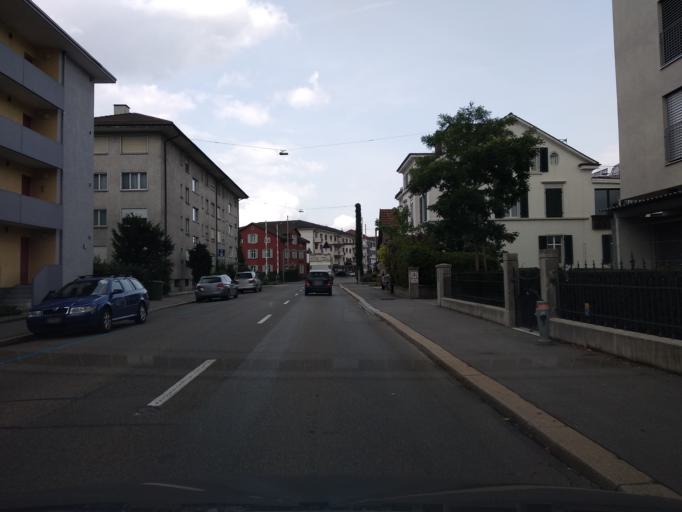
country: CH
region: Zurich
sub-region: Bezirk Winterthur
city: Winterthur
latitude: 47.5064
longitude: 8.7236
